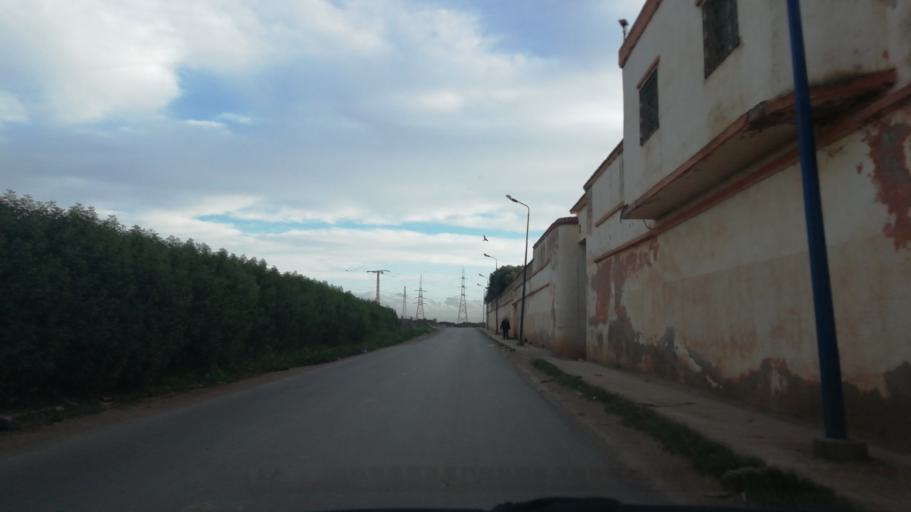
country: DZ
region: Oran
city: Es Senia
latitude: 35.6816
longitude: -0.5865
